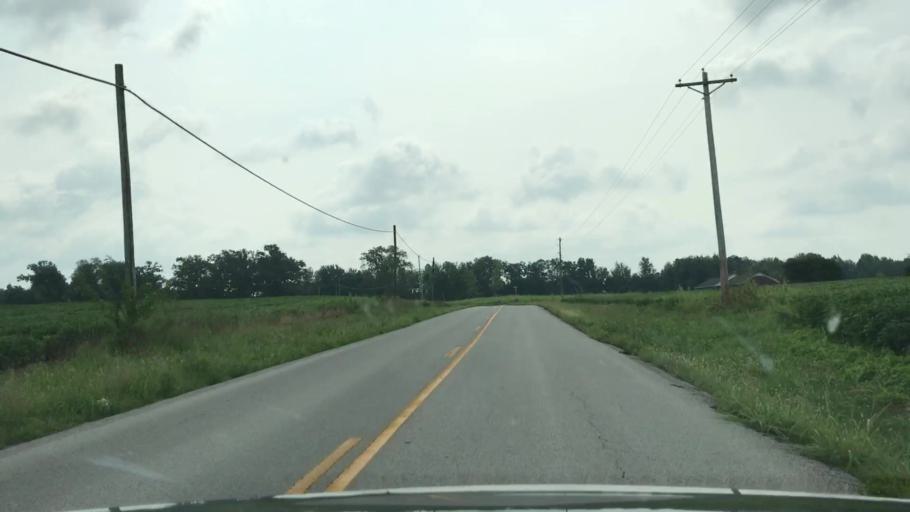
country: US
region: Kentucky
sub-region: Edmonson County
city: Brownsville
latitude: 37.1528
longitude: -86.2068
